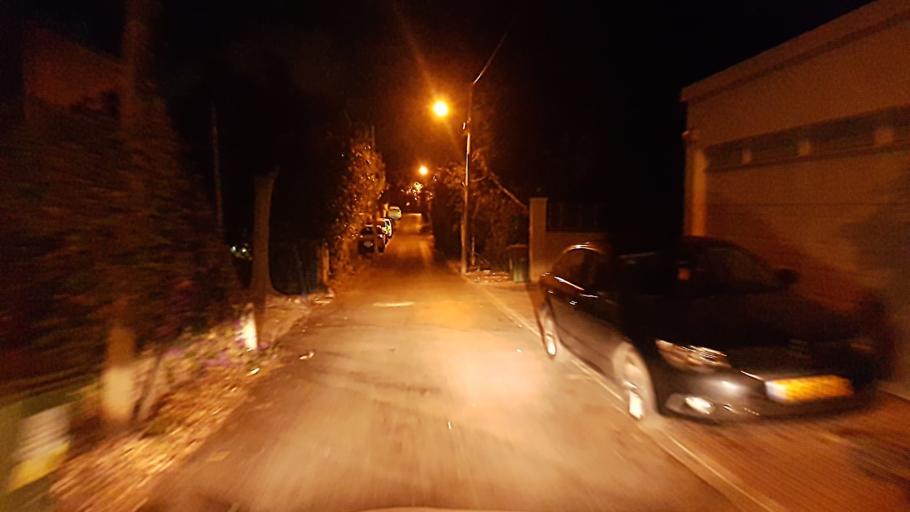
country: IL
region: Central District
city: Hod HaSharon
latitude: 32.1631
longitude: 34.8767
